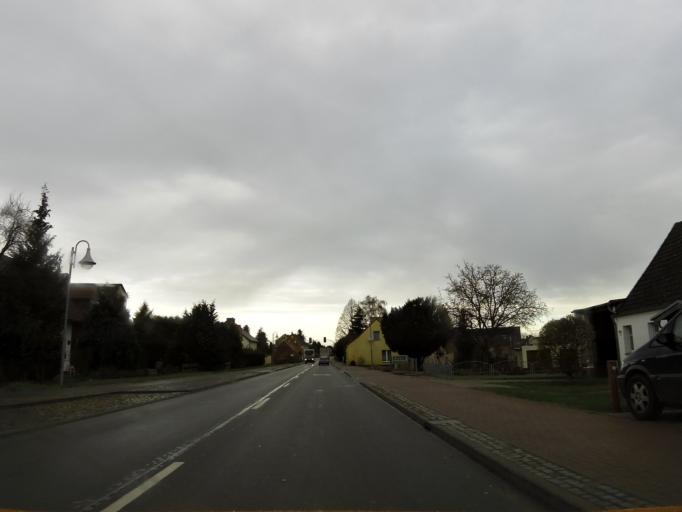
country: DE
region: Saxony-Anhalt
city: Gardelegen
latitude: 52.5745
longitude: 11.3597
